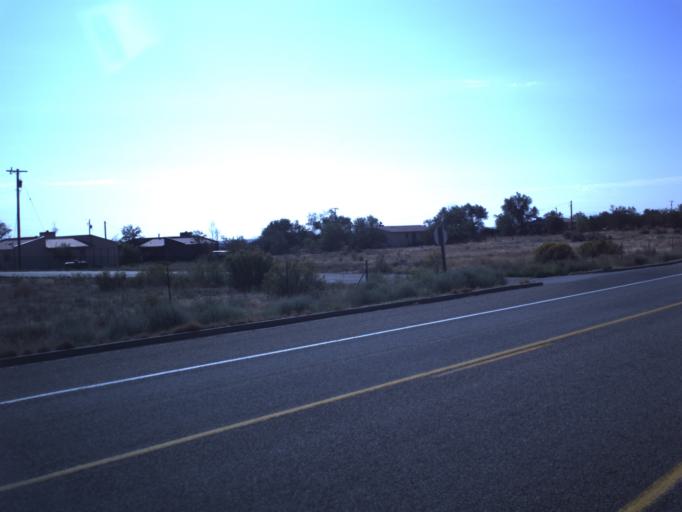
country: US
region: Utah
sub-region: San Juan County
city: Blanding
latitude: 37.4638
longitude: -109.4671
